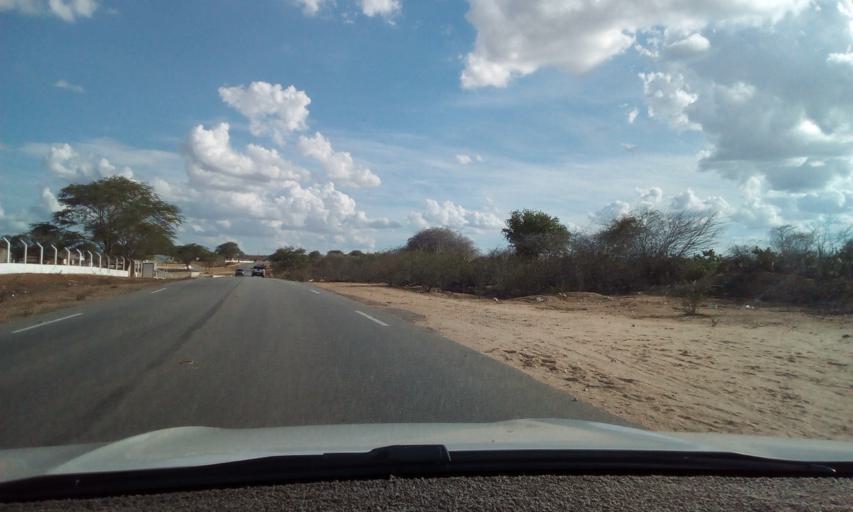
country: BR
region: Paraiba
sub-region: Soledade
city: Soledade
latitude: -6.9193
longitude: -36.3860
